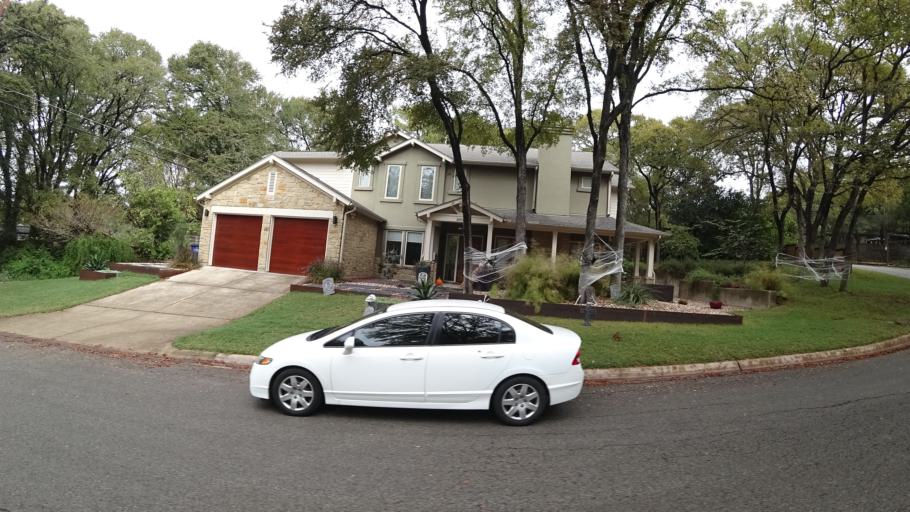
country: US
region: Texas
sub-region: Travis County
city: Rollingwood
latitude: 30.2478
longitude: -97.7821
